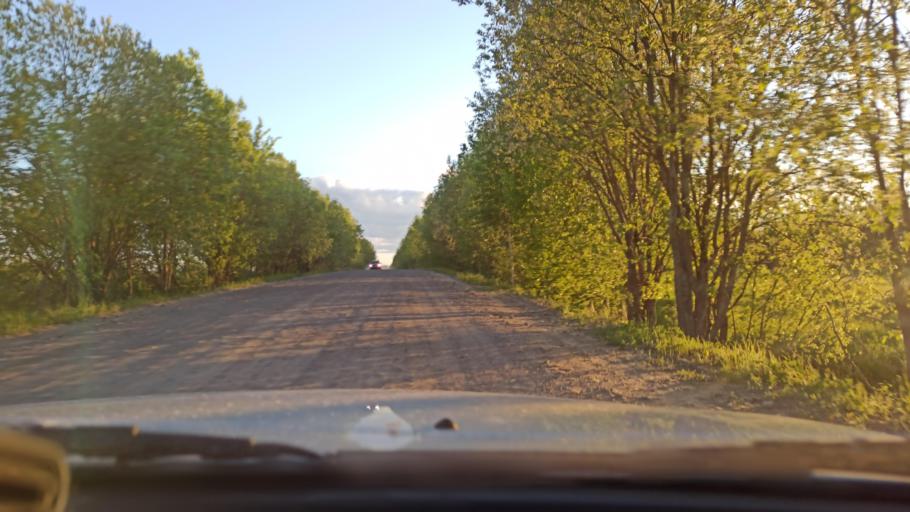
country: RU
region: Vologda
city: Molochnoye
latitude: 59.3707
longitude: 39.6901
